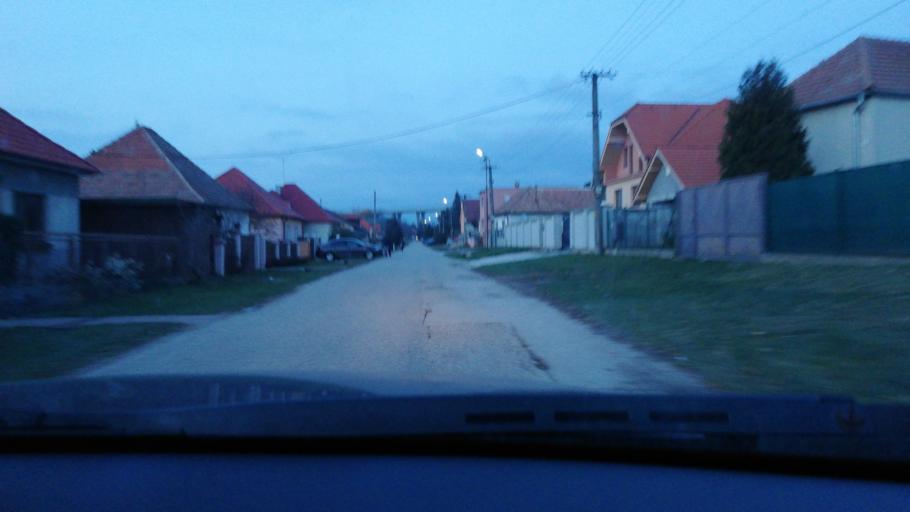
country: SK
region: Nitriansky
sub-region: Okres Nitra
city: Nitra
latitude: 48.3130
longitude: 17.9933
